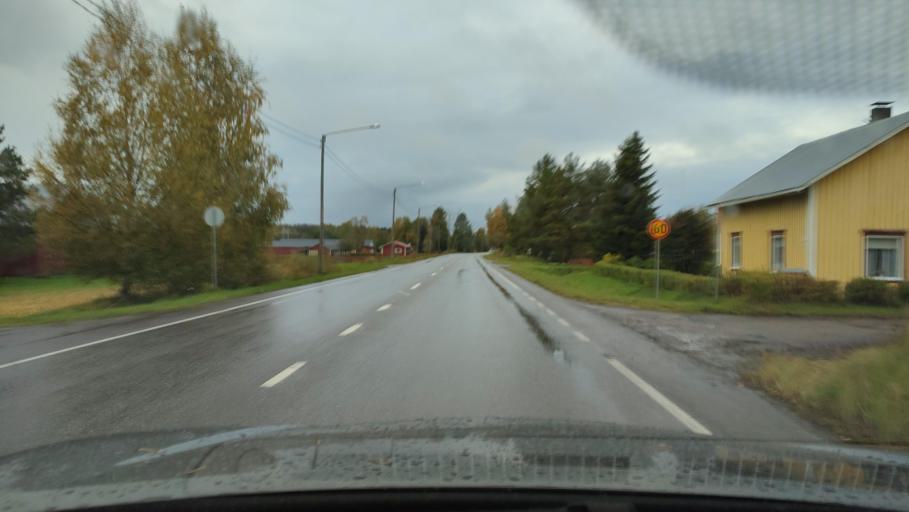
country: FI
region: Southern Ostrobothnia
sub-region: Suupohja
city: Karijoki
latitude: 62.2303
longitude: 21.6271
